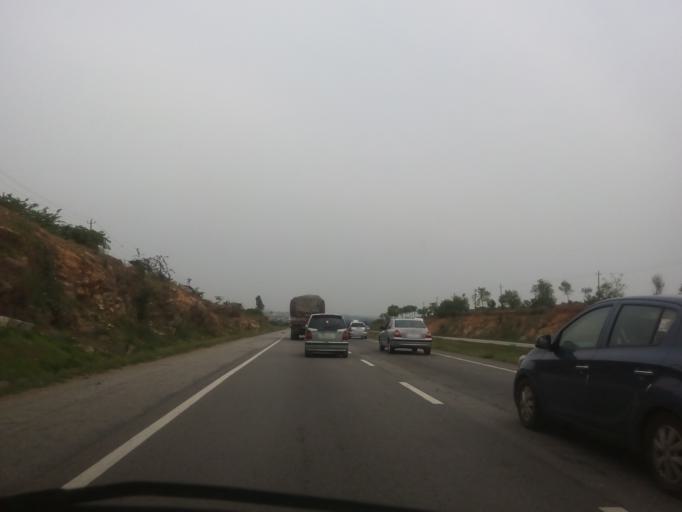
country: IN
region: Karnataka
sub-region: Bangalore Urban
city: Bangalore
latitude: 12.9621
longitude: 77.4715
